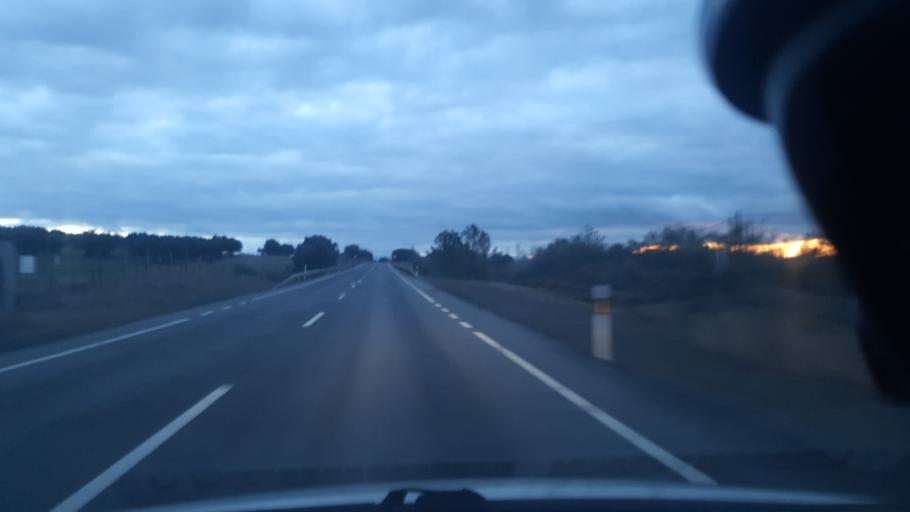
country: ES
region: Castille and Leon
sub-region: Provincia de Avila
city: Ojos-Albos
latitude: 40.7297
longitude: -4.5093
